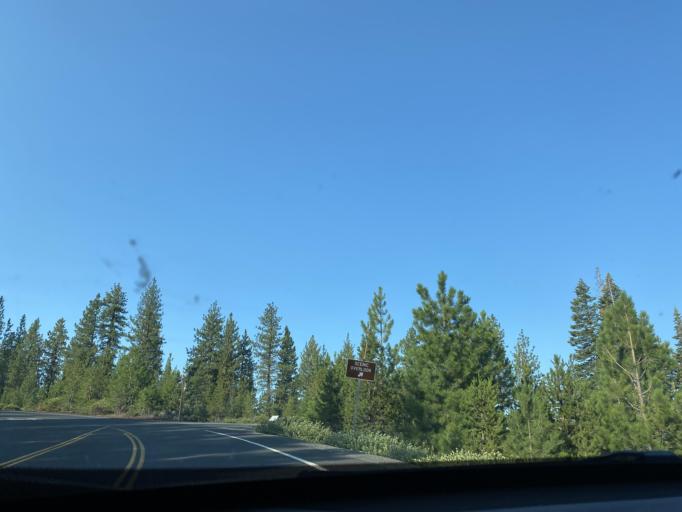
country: US
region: Oregon
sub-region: Deschutes County
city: La Pine
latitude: 43.7046
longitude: -121.3170
